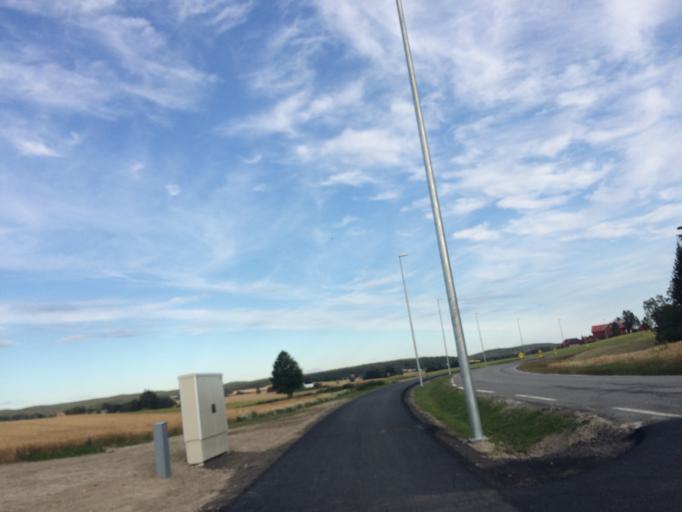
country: NO
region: Akershus
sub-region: Ski
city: Ski
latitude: 59.6962
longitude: 10.8565
